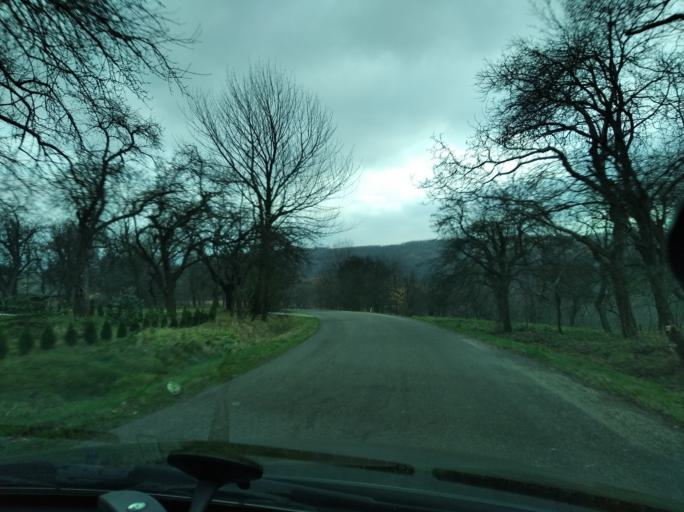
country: PL
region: Subcarpathian Voivodeship
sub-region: Powiat przeworski
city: Sietesz
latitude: 49.9696
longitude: 22.3391
